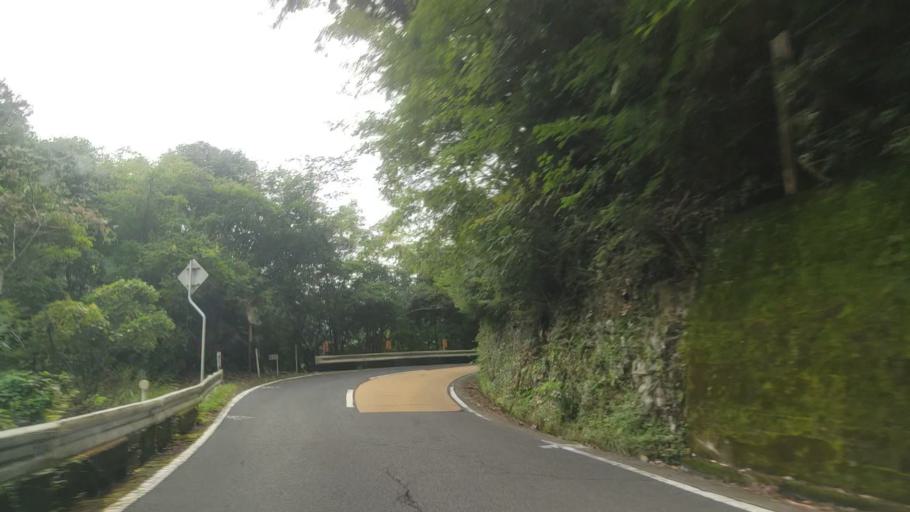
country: JP
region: Wakayama
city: Koya
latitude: 34.2442
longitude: 135.5479
